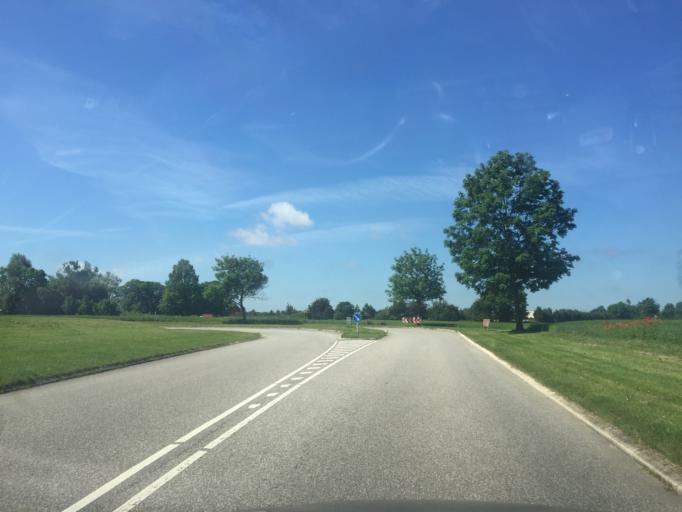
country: DK
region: Capital Region
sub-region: Hoje-Taastrup Kommune
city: Flong
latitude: 55.6641
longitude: 12.1738
